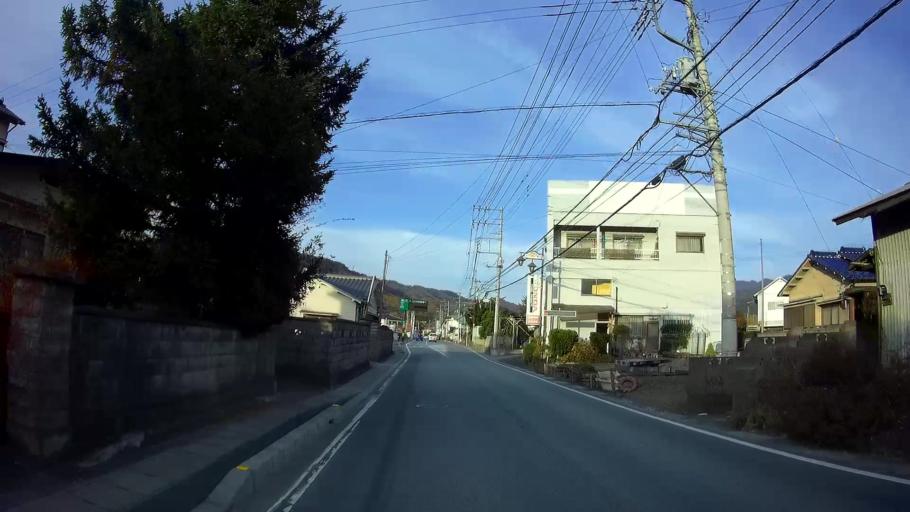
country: JP
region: Yamanashi
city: Ryuo
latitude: 35.4879
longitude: 138.4588
